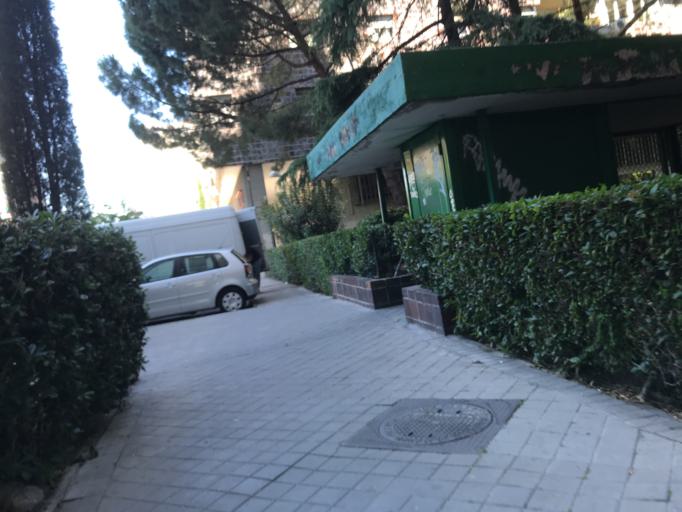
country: ES
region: Madrid
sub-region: Provincia de Madrid
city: Retiro
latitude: 40.4152
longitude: -3.6720
